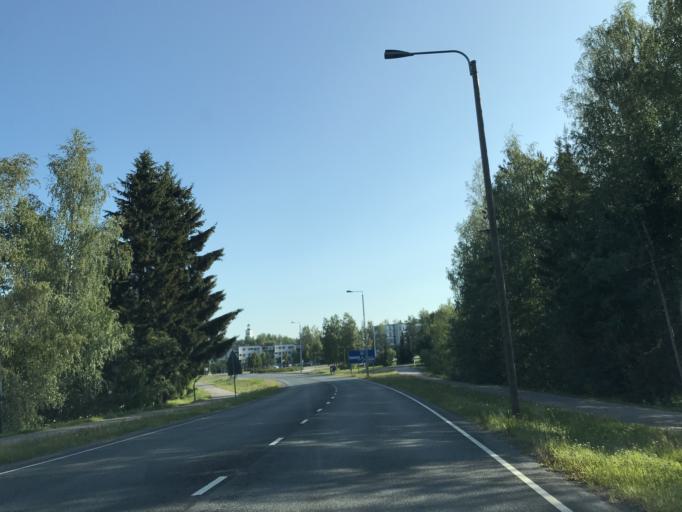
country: FI
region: Paijanne Tavastia
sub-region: Lahti
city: Orimattila
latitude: 60.8001
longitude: 25.7277
